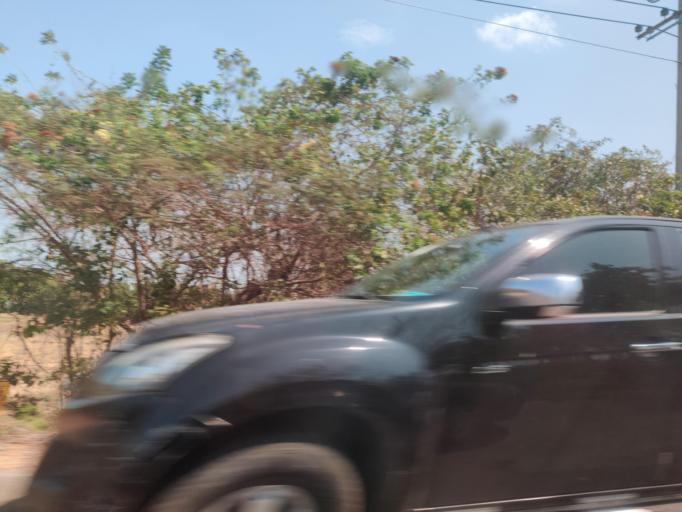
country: CO
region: Bolivar
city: Turbana
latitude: 10.2755
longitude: -75.5452
